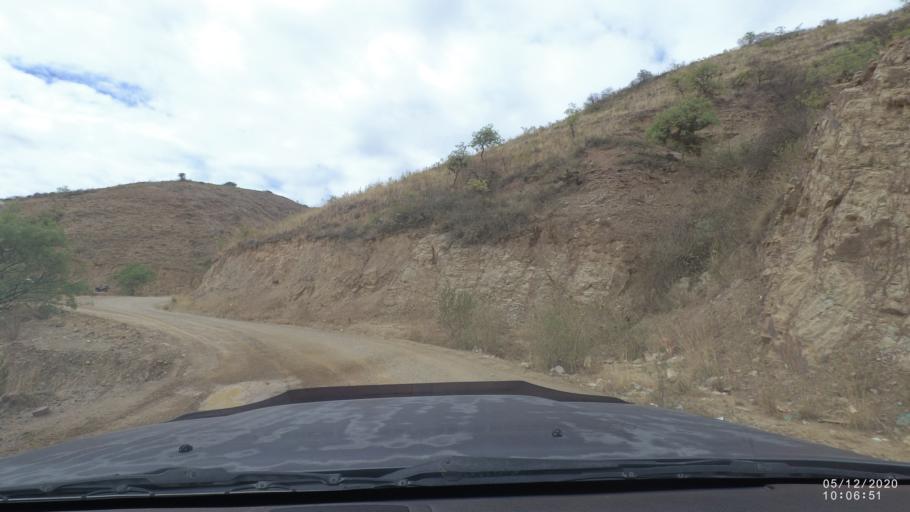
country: BO
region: Cochabamba
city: Sipe Sipe
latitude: -17.4782
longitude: -66.2843
